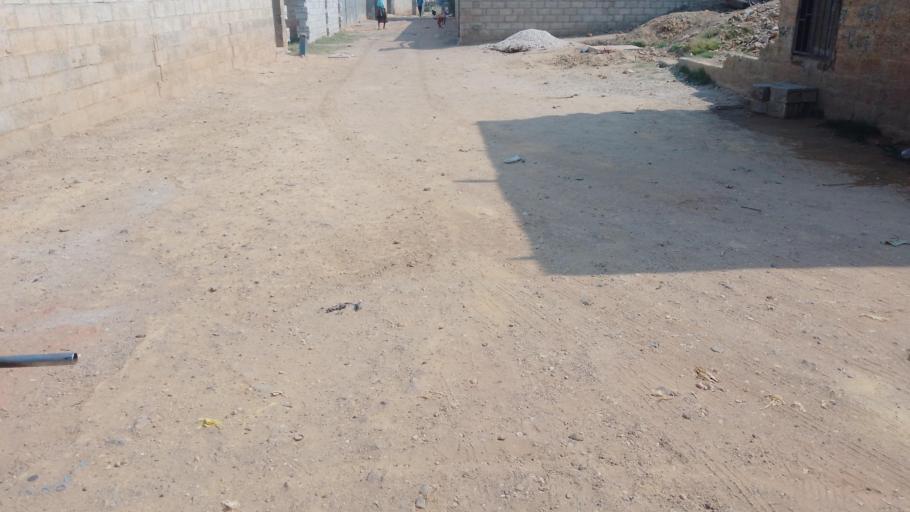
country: ZM
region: Lusaka
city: Lusaka
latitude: -15.4021
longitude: 28.3651
